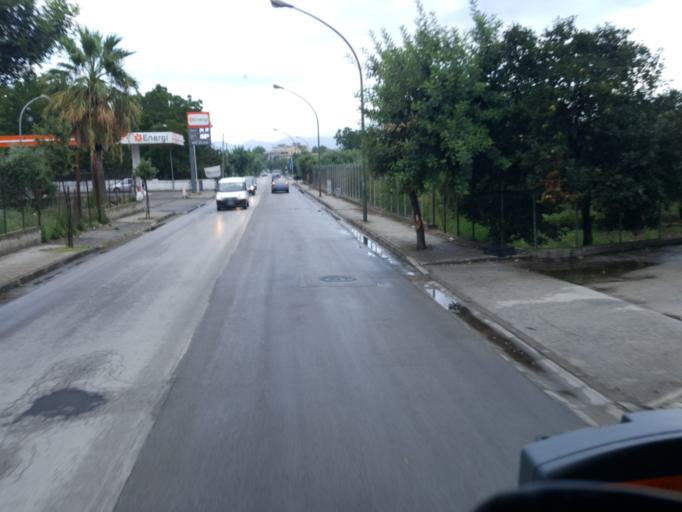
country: IT
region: Campania
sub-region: Provincia di Napoli
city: Palma Campania
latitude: 40.8632
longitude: 14.5486
